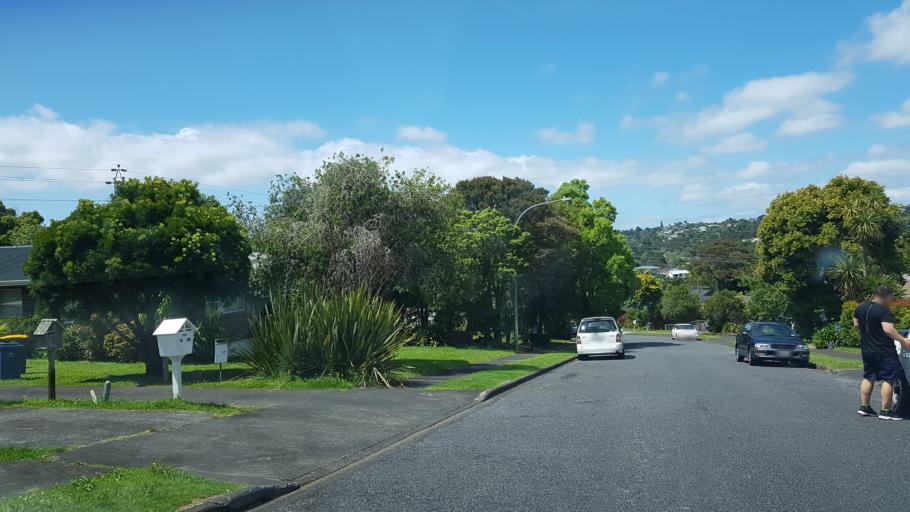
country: NZ
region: Auckland
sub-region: Auckland
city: North Shore
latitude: -36.7923
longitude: 174.7143
